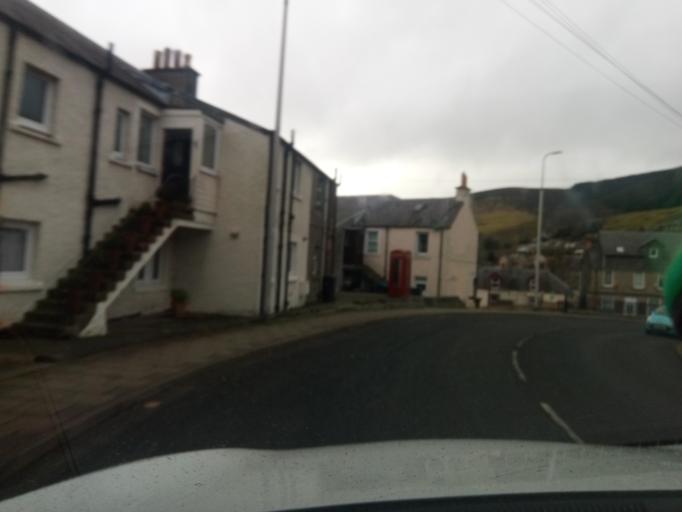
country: GB
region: Scotland
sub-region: The Scottish Borders
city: Innerleithen
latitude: 55.6236
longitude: -3.0193
